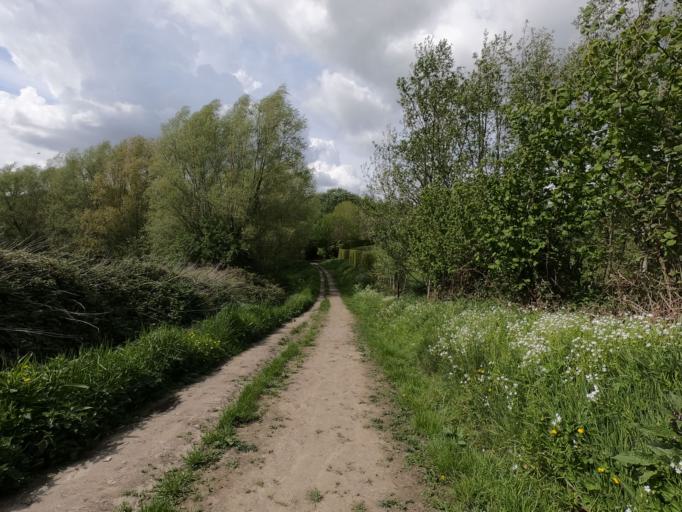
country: BE
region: Flanders
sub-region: Provincie Oost-Vlaanderen
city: Ronse
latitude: 50.7896
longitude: 3.5844
